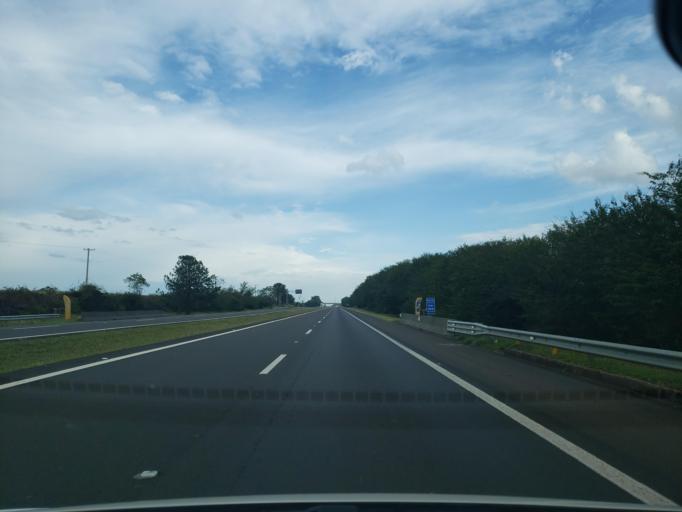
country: BR
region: Sao Paulo
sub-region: Itirapina
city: Itirapina
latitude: -22.2663
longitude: -47.9223
